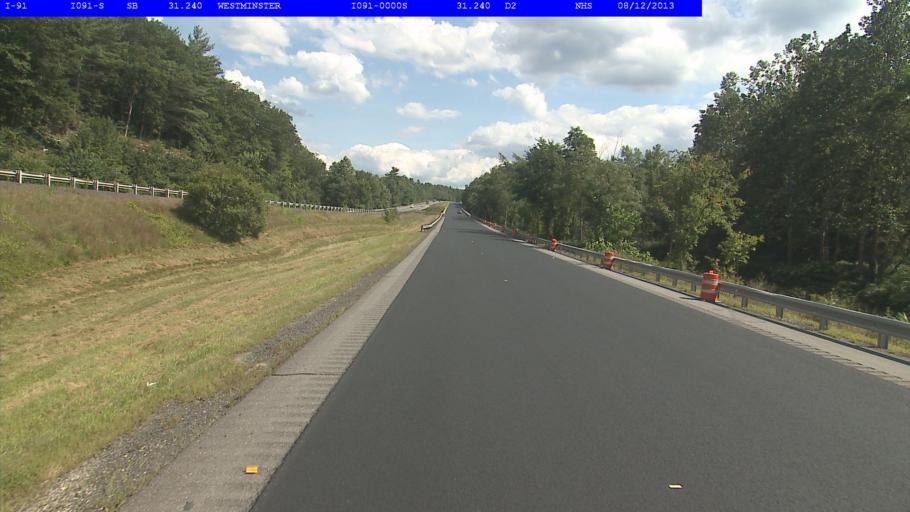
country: US
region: Vermont
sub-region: Windham County
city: Bellows Falls
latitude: 43.1253
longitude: -72.4710
